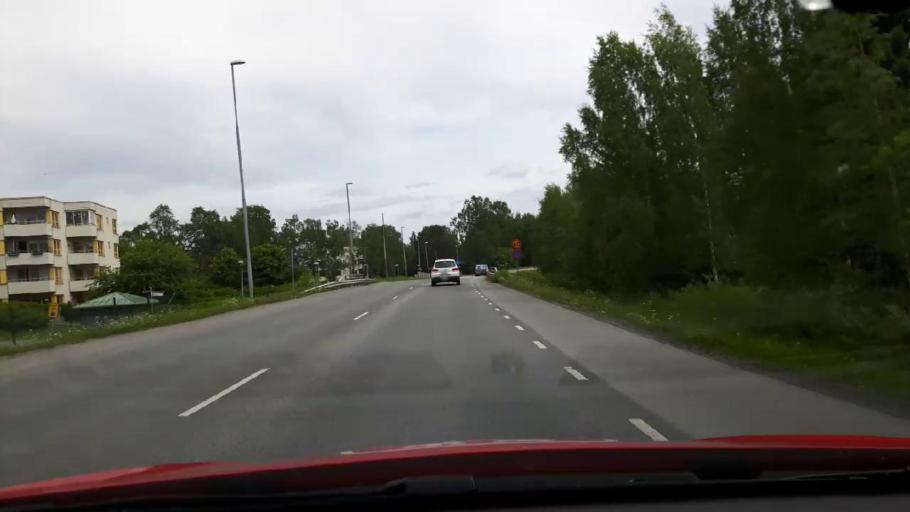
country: SE
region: Jaemtland
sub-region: Krokoms Kommun
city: Krokom
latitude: 63.1173
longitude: 14.4322
